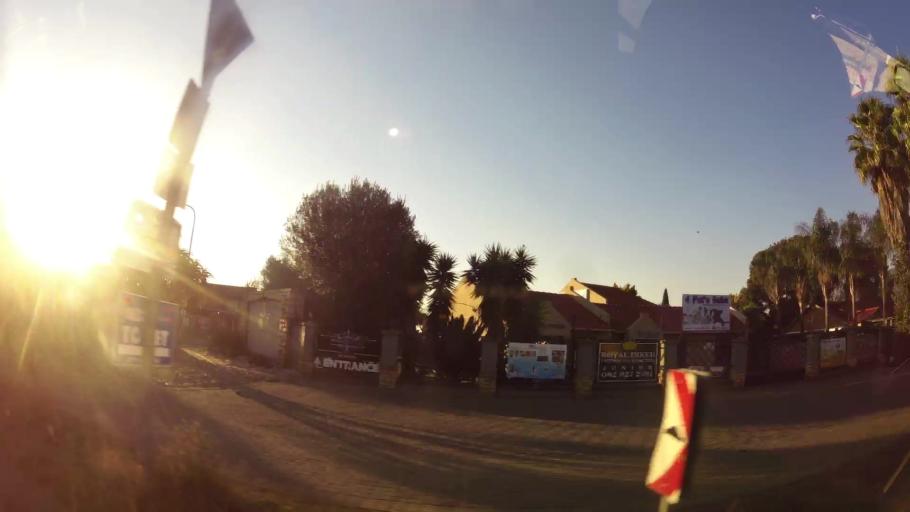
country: ZA
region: Gauteng
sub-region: City of Tshwane Metropolitan Municipality
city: Centurion
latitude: -25.8723
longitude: 28.1570
